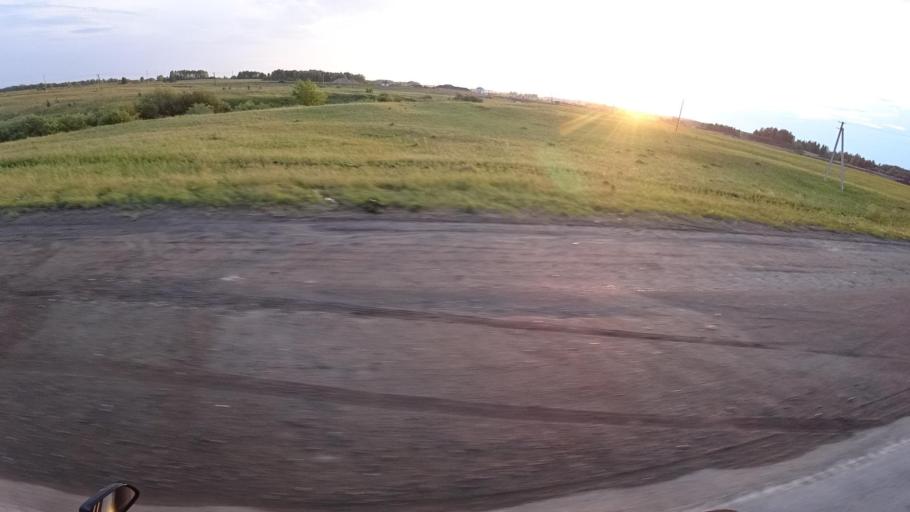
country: RU
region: Sverdlovsk
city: Kamyshlov
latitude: 56.8746
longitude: 62.7118
